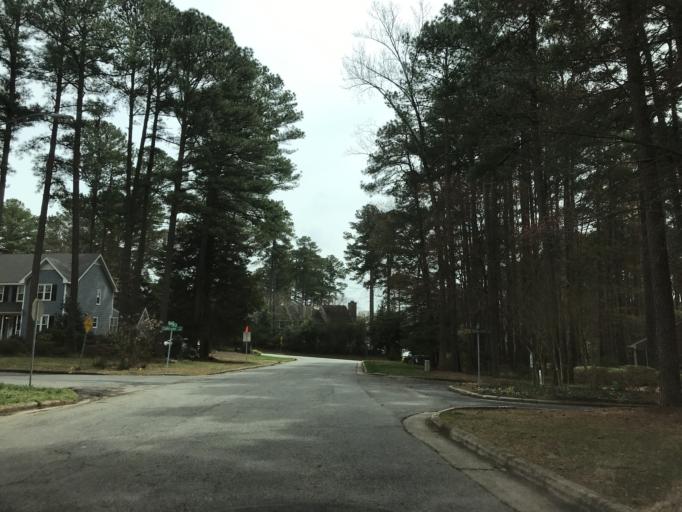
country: US
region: North Carolina
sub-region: Wake County
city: West Raleigh
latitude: 35.8854
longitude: -78.6709
